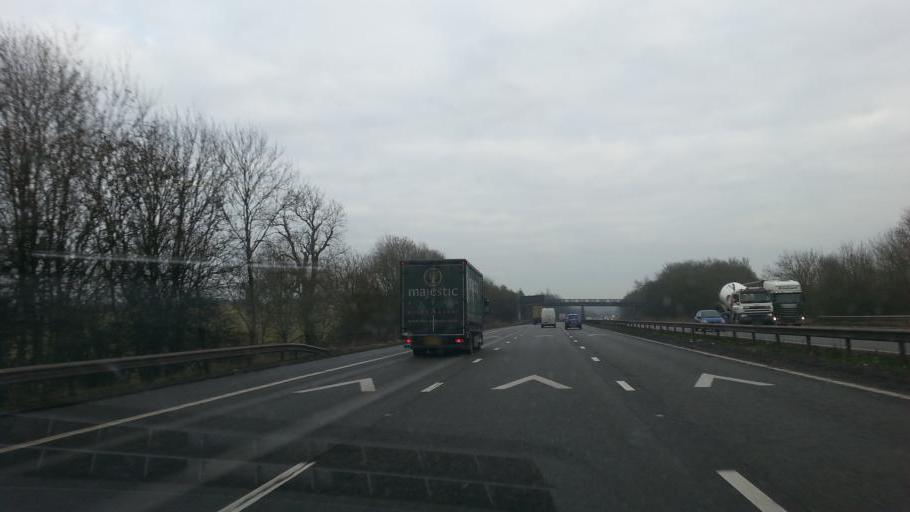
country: GB
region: England
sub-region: Warwickshire
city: Long Lawford
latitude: 52.4342
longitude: -1.3467
